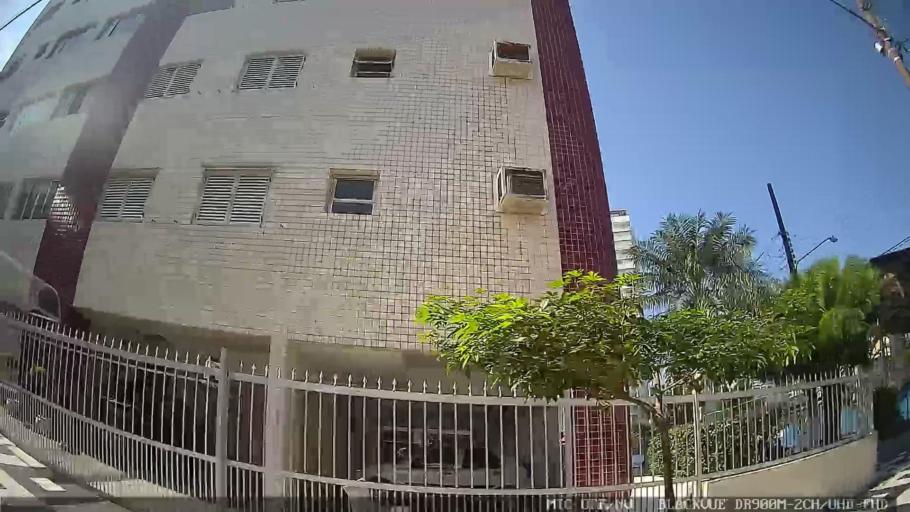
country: BR
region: Sao Paulo
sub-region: Guaruja
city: Guaruja
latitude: -24.0065
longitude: -46.2721
